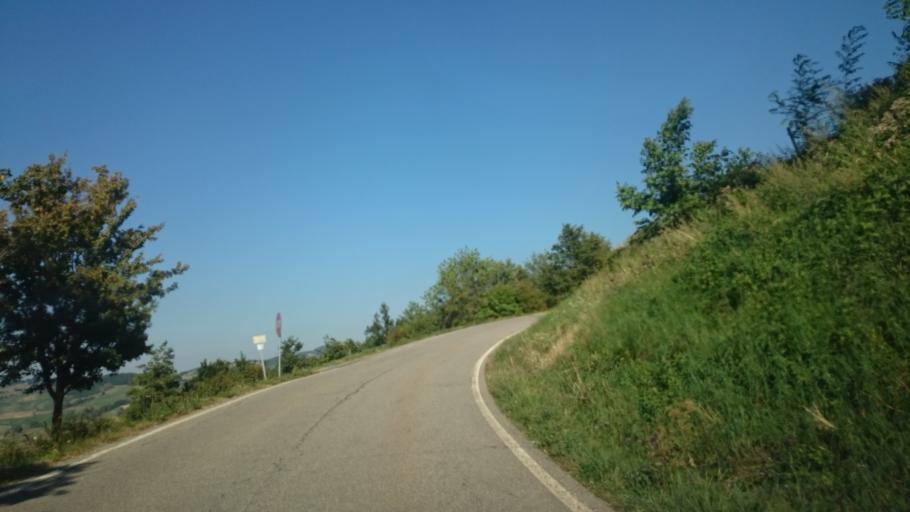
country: IT
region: Emilia-Romagna
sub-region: Provincia di Reggio Emilia
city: Villa Minozzo
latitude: 44.3492
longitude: 10.4881
